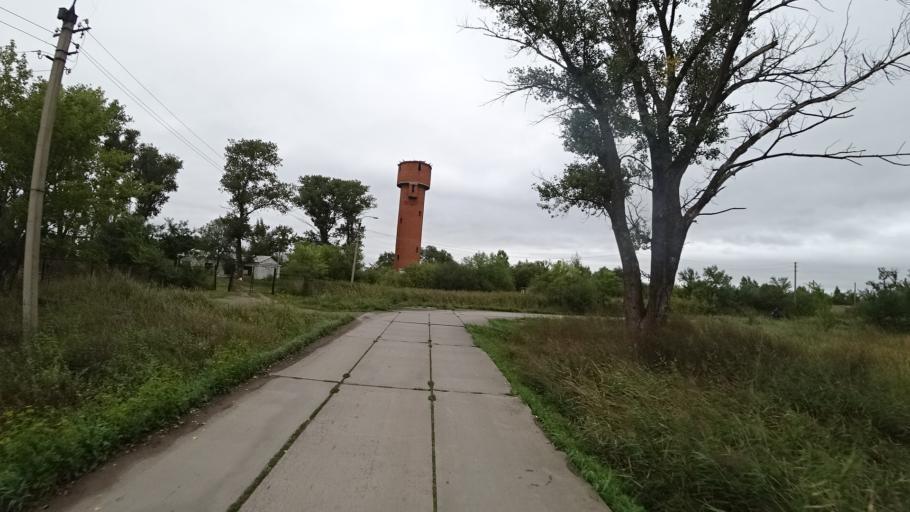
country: RU
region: Primorskiy
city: Chernigovka
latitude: 44.3345
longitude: 132.5381
